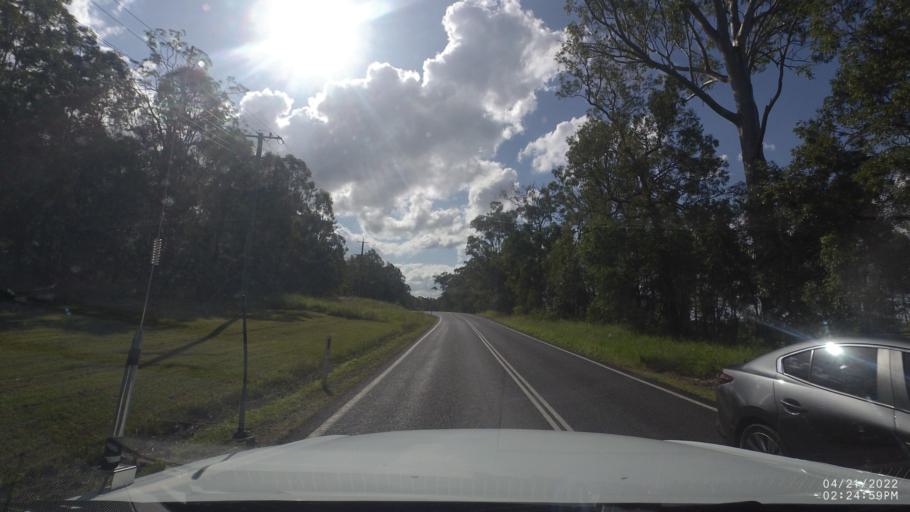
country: AU
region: Queensland
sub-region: Logan
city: Chambers Flat
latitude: -27.8202
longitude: 153.0998
